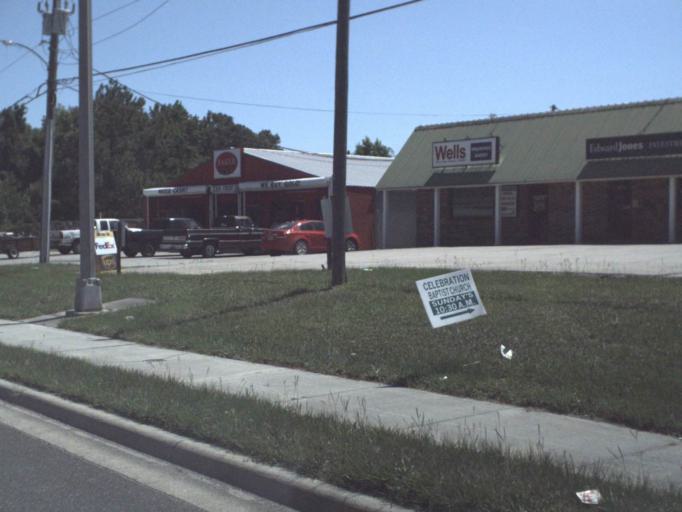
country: US
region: Florida
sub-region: Baker County
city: Macclenny
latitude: 30.2671
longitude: -82.1226
